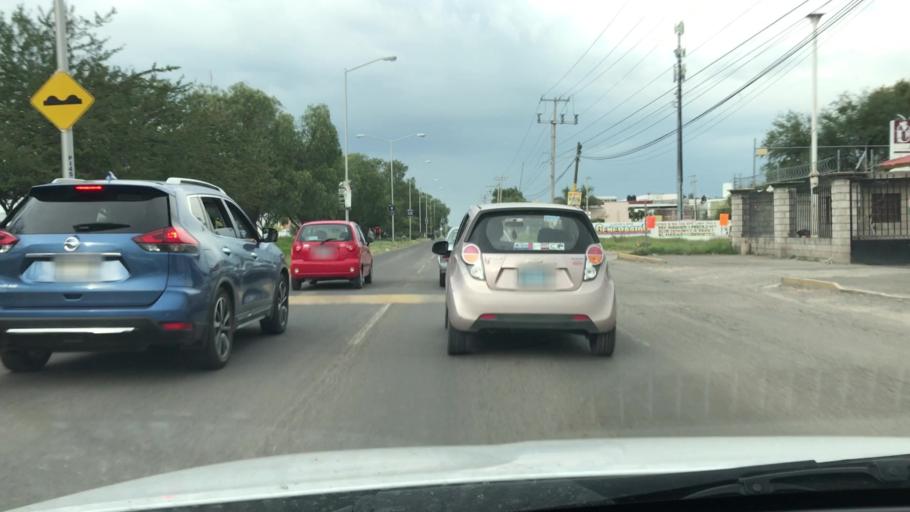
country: MX
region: Guanajuato
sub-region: Celaya
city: La Trinidad
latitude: 20.5364
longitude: -100.7902
